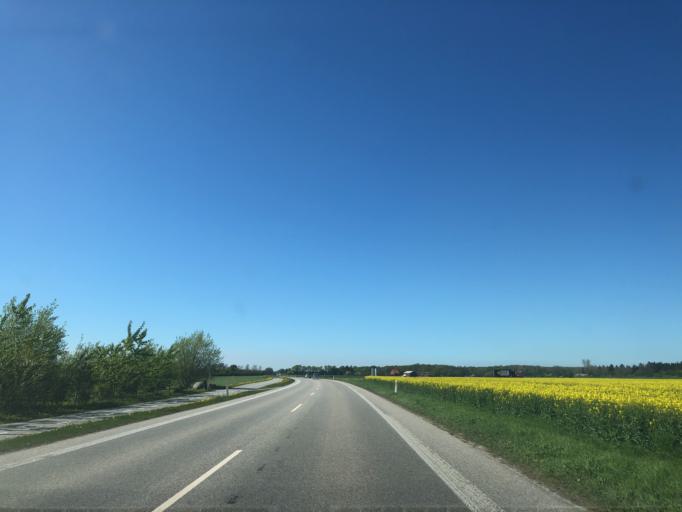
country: DK
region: Zealand
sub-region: Stevns Kommune
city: Store Heddinge
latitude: 55.3305
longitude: 12.3609
